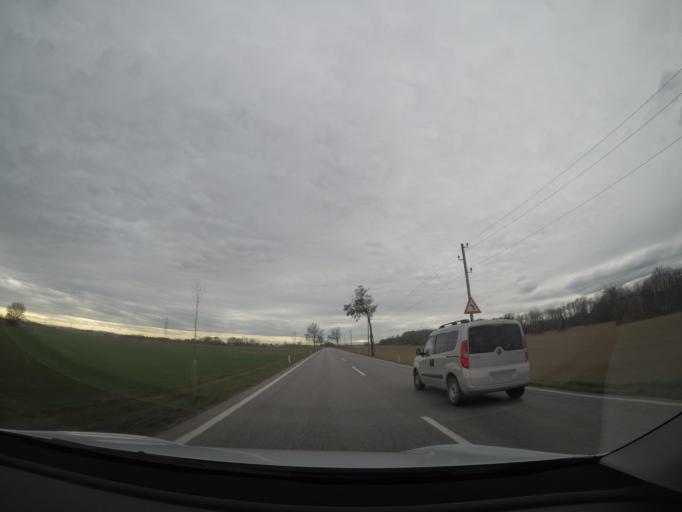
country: AT
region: Lower Austria
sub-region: Politischer Bezirk Modling
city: Achau
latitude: 48.0709
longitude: 16.3842
